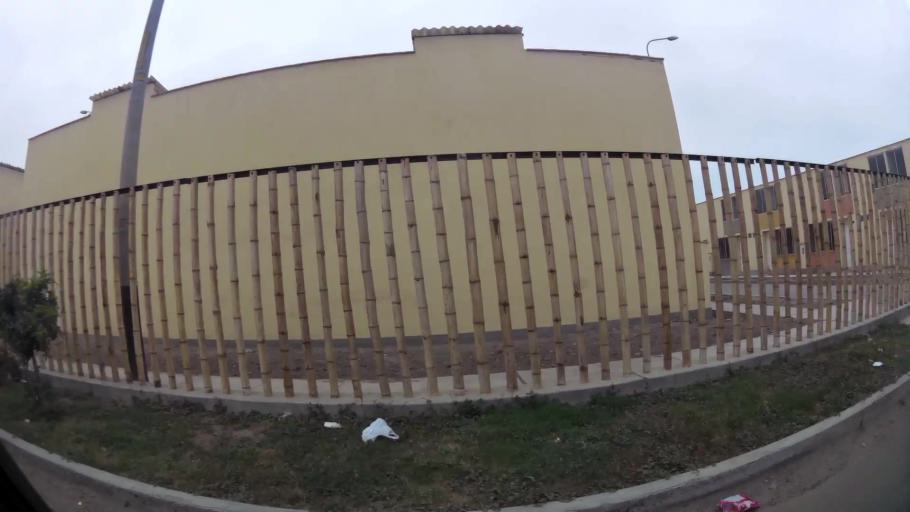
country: PE
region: La Libertad
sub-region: Provincia de Trujillo
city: Buenos Aires
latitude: -8.1437
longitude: -79.0458
